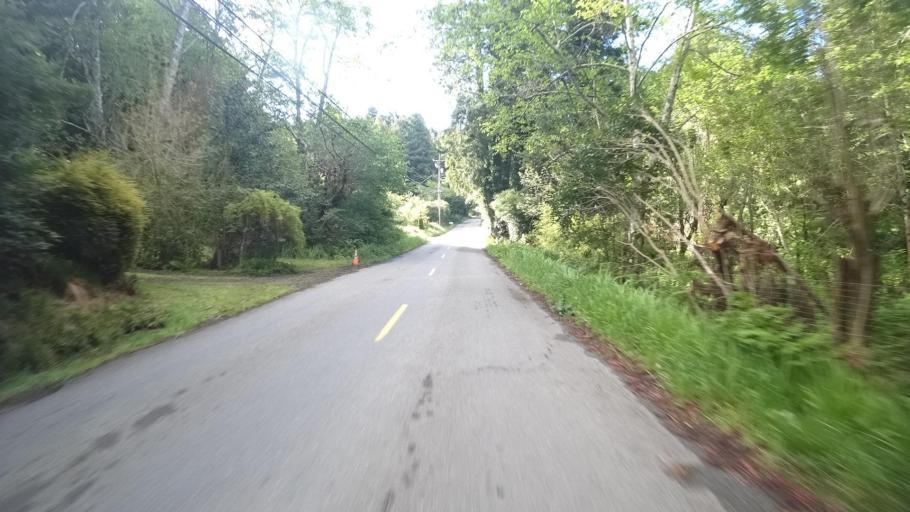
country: US
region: California
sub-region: Humboldt County
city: Westhaven-Moonstone
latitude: 41.0403
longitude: -124.1091
